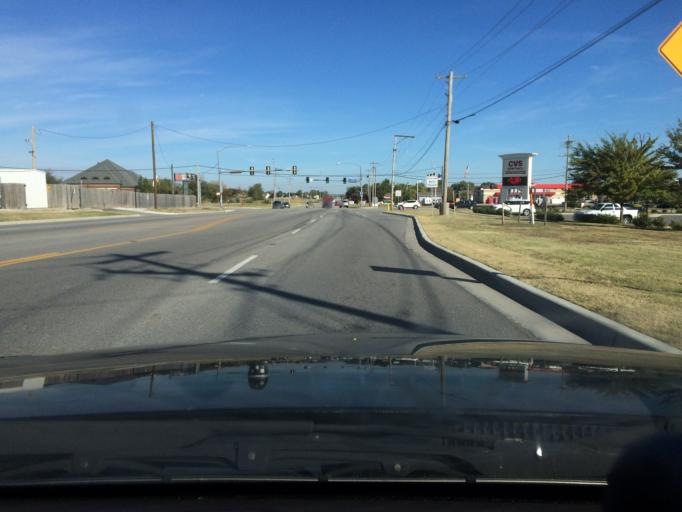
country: US
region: Oklahoma
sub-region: Tulsa County
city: Broken Arrow
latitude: 36.0744
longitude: -95.7796
